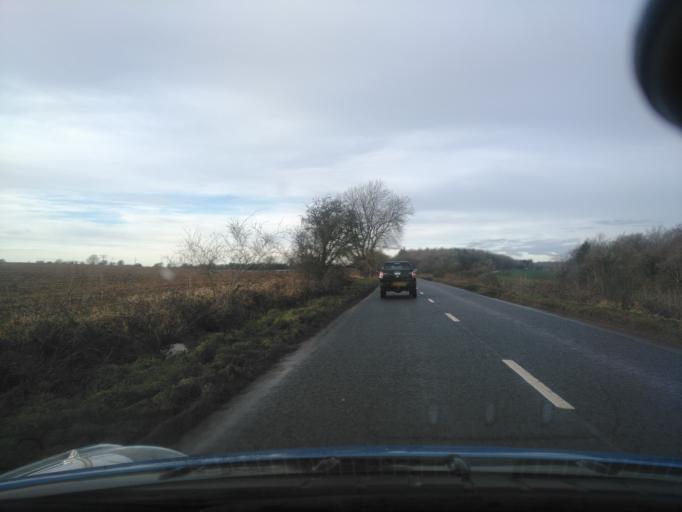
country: GB
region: England
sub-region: Gloucestershire
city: Chipping Campden
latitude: 51.9940
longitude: -1.7720
